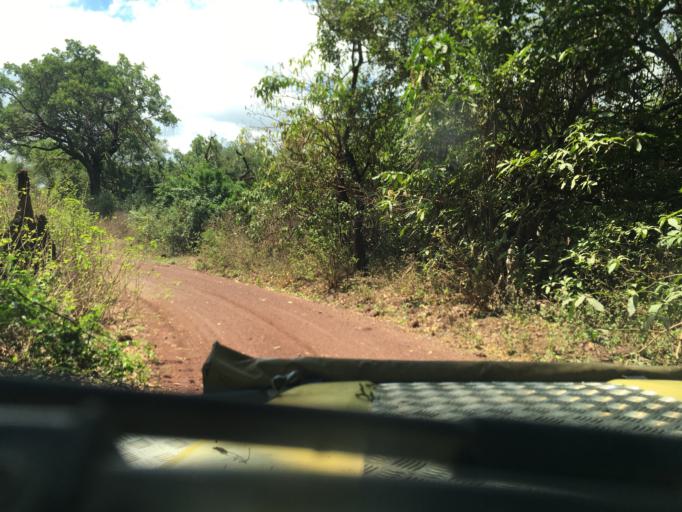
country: TZ
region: Arusha
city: Mto wa Mbu
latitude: -3.4198
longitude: 35.8141
